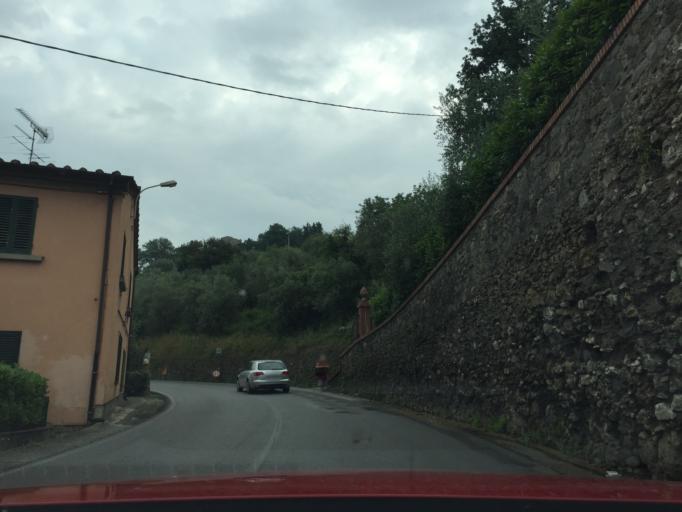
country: IT
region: Tuscany
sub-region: Provincia di Pistoia
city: Serravalle Pistoiese
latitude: 43.8990
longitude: 10.8251
